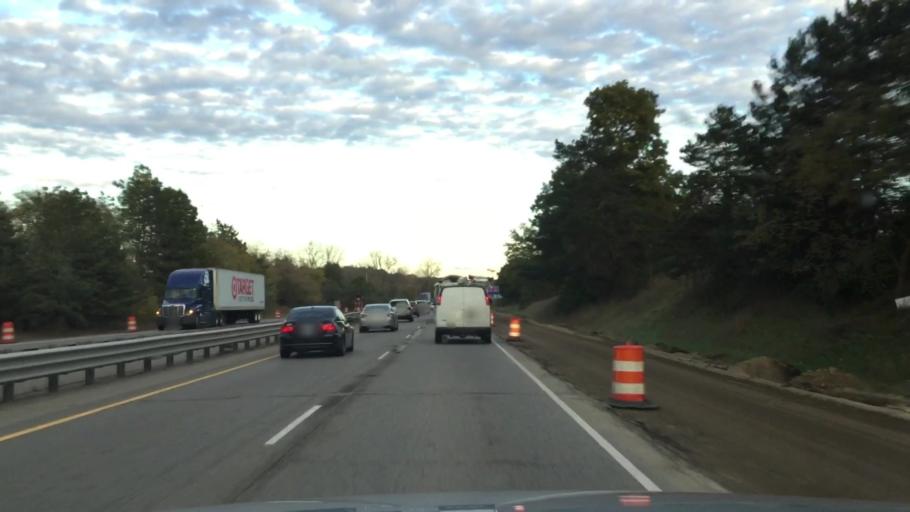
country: US
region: Michigan
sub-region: Jackson County
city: Michigan Center
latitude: 42.2774
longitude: -84.3287
